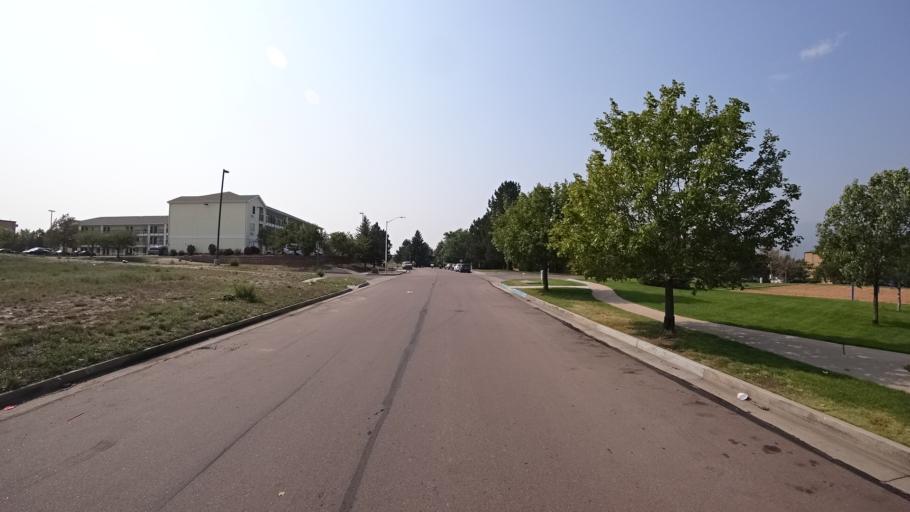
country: US
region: Colorado
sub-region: El Paso County
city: Stratmoor
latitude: 38.8165
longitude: -104.7620
